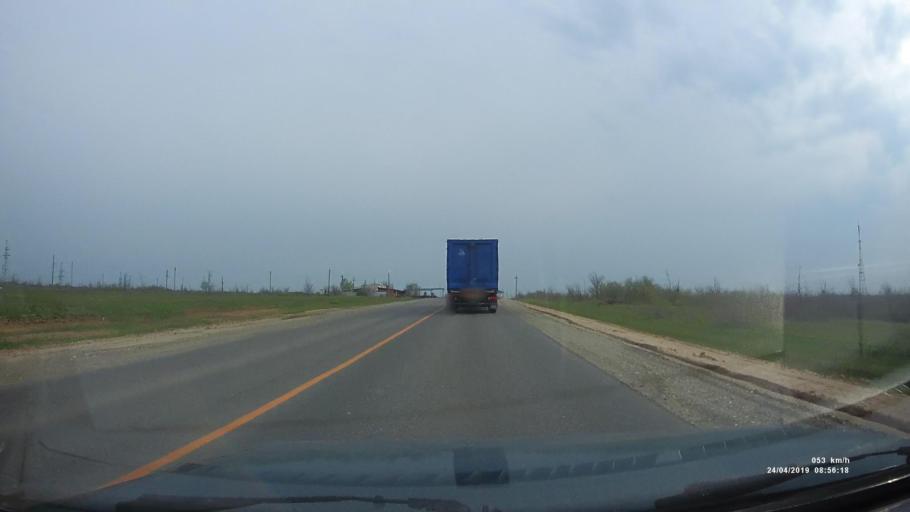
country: RU
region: Kalmykiya
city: Arshan'
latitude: 46.3007
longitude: 44.1839
